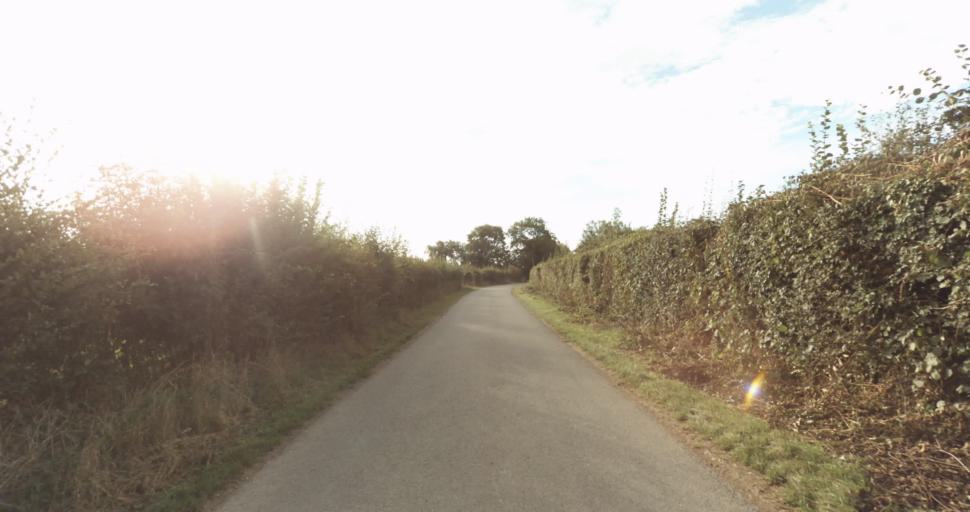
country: FR
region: Lower Normandy
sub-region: Departement de l'Orne
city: Vimoutiers
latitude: 48.8865
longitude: 0.2397
